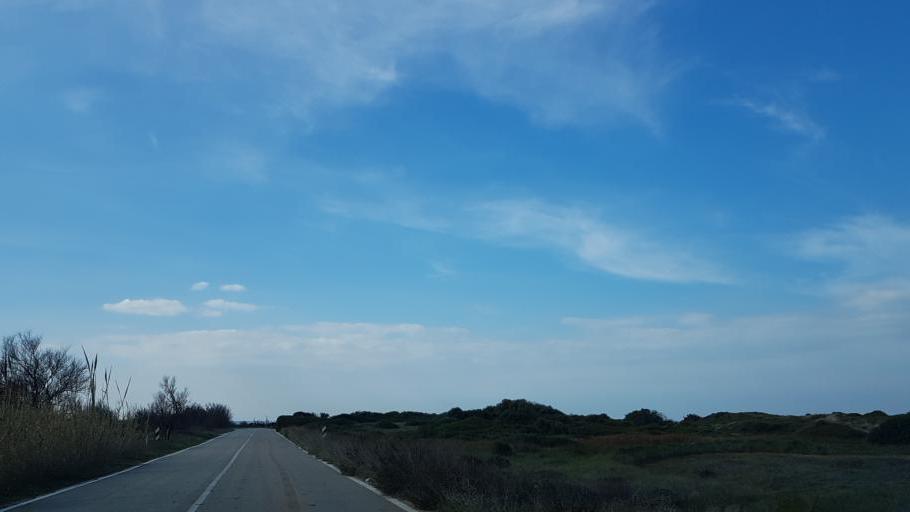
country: IT
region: Apulia
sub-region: Provincia di Brindisi
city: Brindisi
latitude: 40.6879
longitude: 17.8558
